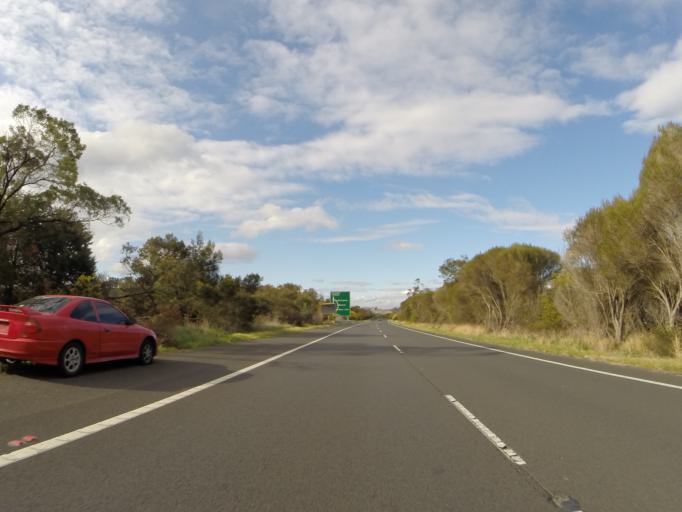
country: AU
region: New South Wales
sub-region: Wingecarribee
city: Bundanoon
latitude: -34.5953
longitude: 150.2413
